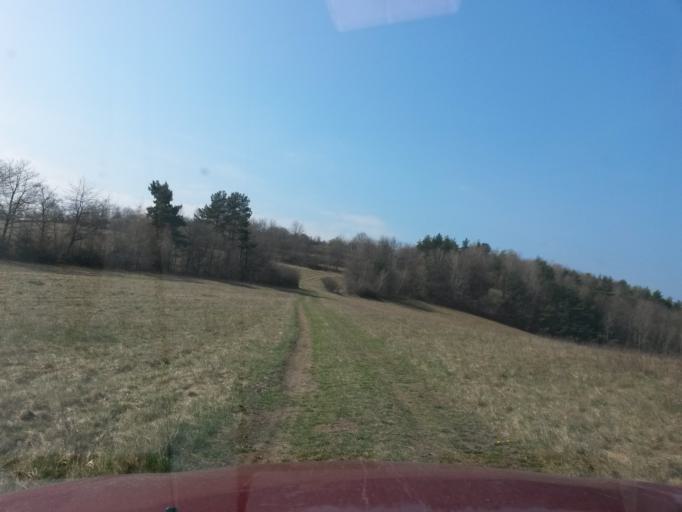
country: SK
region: Presovsky
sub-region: Okres Presov
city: Presov
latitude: 48.9276
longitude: 21.1490
